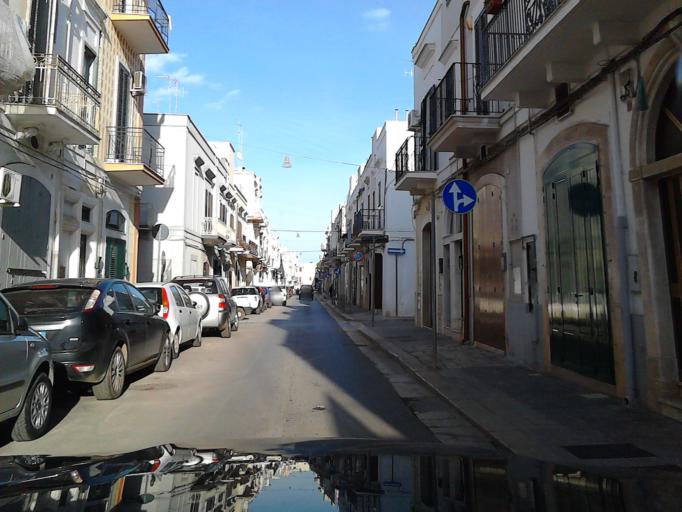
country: IT
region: Apulia
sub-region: Provincia di Bari
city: Mola di Bari
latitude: 41.0567
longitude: 17.0860
